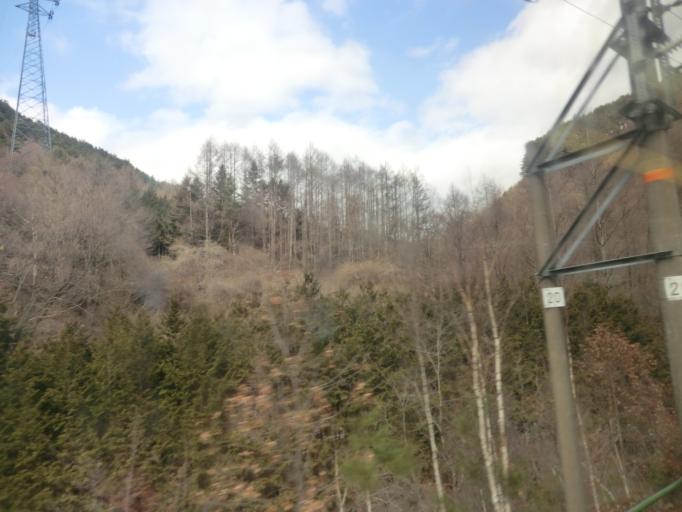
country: JP
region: Nagano
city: Ina
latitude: 35.9520
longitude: 137.7854
